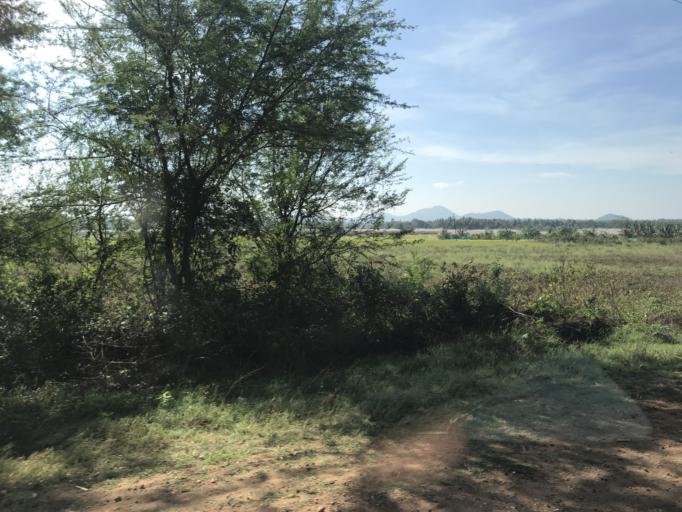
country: IN
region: Karnataka
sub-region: Mysore
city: Heggadadevankote
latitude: 12.1195
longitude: 76.4216
